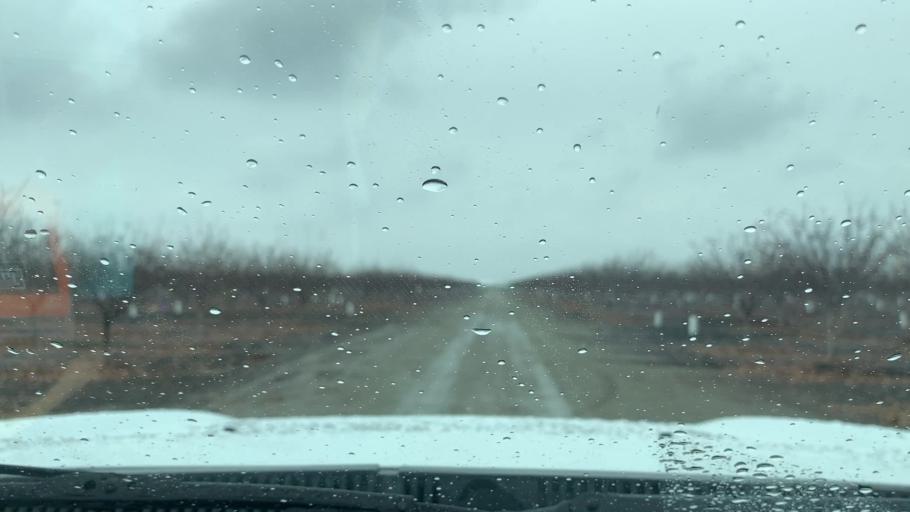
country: US
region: California
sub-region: Kings County
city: Corcoran
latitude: 36.0290
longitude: -119.4962
